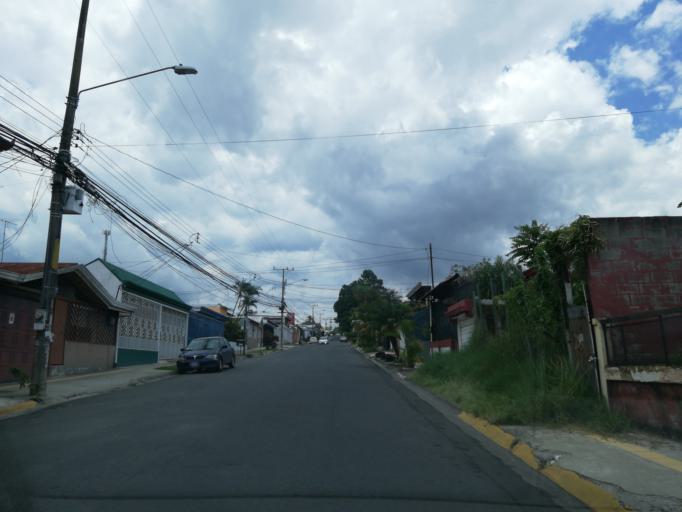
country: CR
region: Alajuela
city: Alajuela
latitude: 10.0126
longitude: -84.2274
